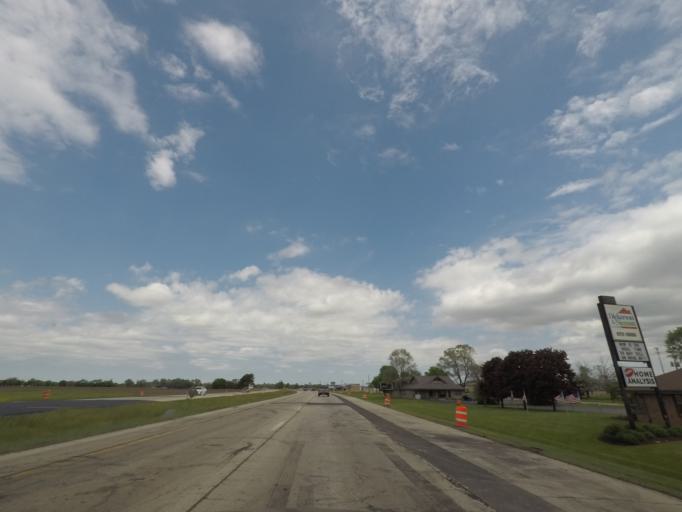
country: US
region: Illinois
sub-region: Winnebago County
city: Roscoe
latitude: 42.4307
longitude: -89.0162
